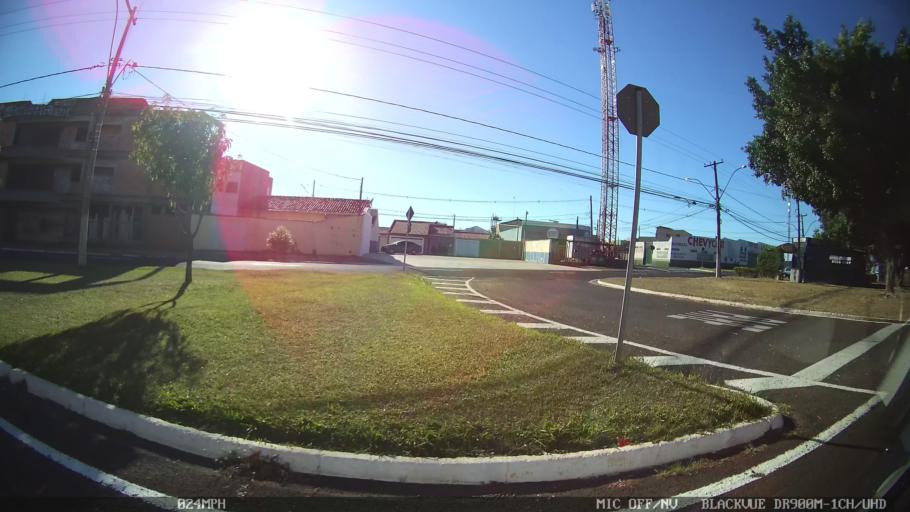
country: BR
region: Sao Paulo
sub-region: Franca
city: Franca
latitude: -20.5633
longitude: -47.3993
